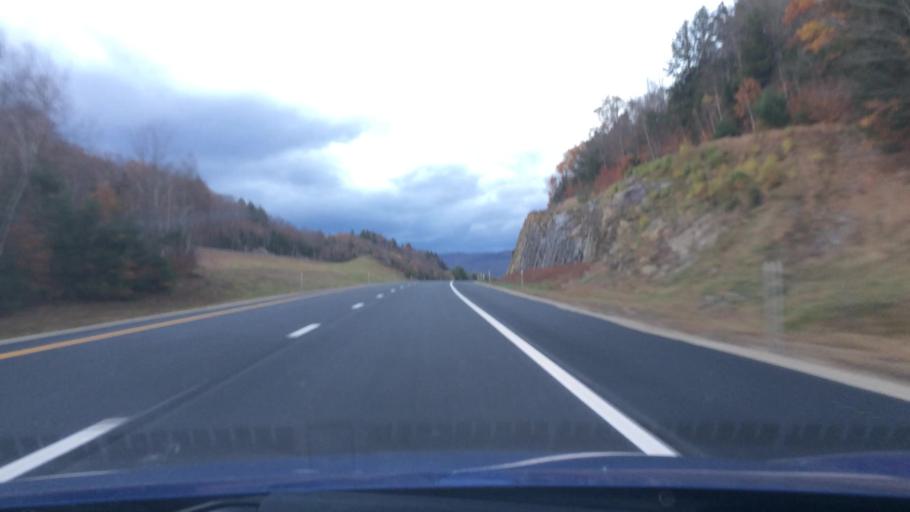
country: US
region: New Hampshire
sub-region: Grafton County
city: Thornton
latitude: 43.8856
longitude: -71.6794
